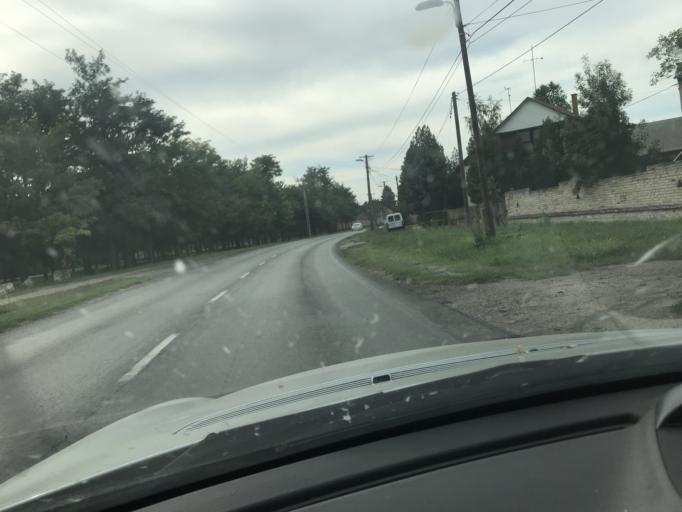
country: HU
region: Bacs-Kiskun
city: Kecel
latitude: 46.5195
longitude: 19.2387
